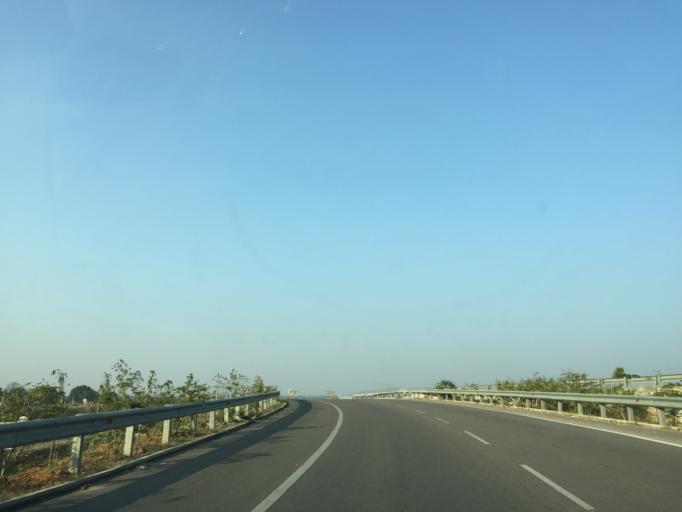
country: IN
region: Telangana
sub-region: Rangareddi
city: Ghatkesar
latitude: 17.4444
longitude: 78.6676
